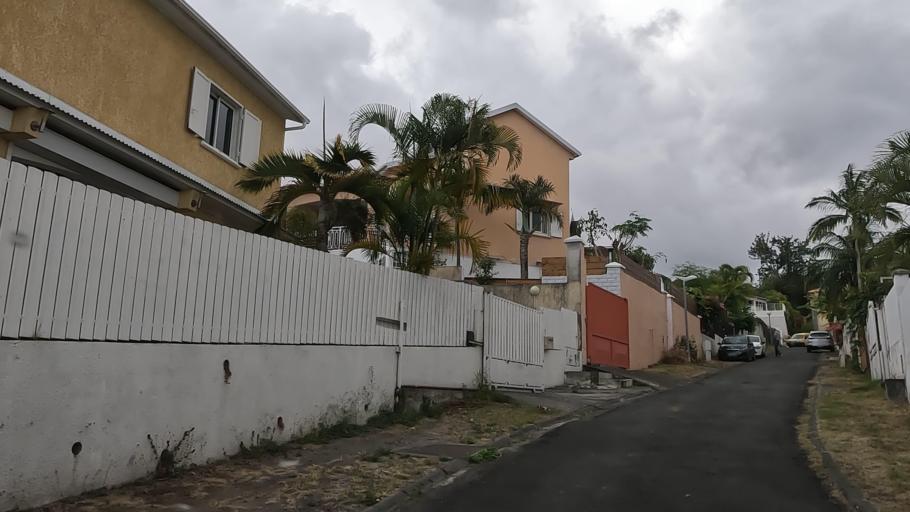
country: RE
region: Reunion
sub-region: Reunion
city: Le Tampon
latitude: -21.2748
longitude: 55.5020
